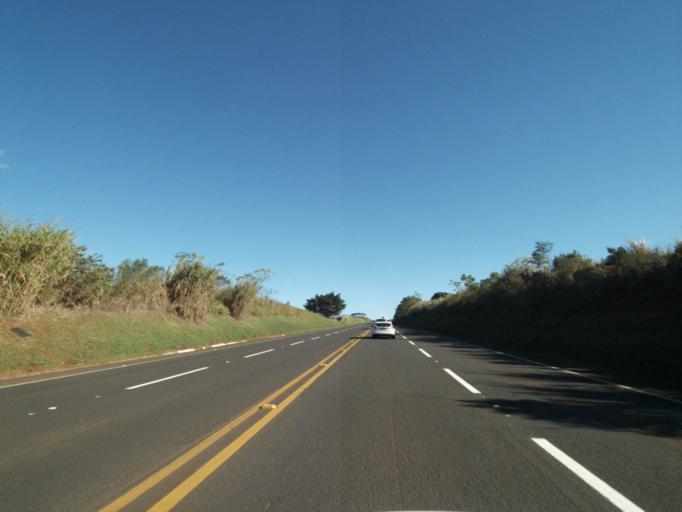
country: BR
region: Parana
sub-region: Mandaguari
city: Mandaguari
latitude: -23.5017
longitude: -51.6504
